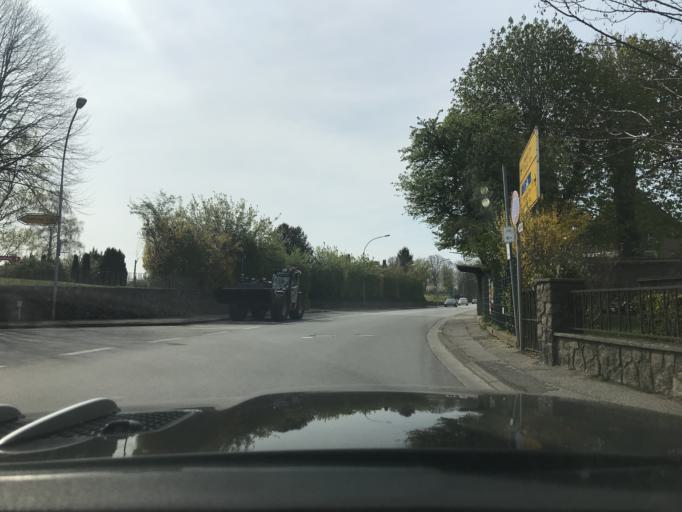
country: DE
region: Schleswig-Holstein
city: Grube
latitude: 54.2299
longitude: 11.0362
